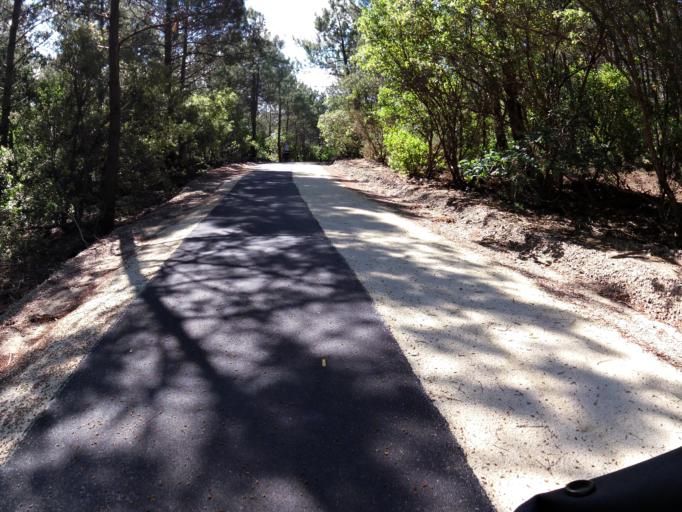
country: FR
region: Aquitaine
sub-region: Departement de la Gironde
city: Lacanau
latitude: 45.0311
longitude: -1.1611
